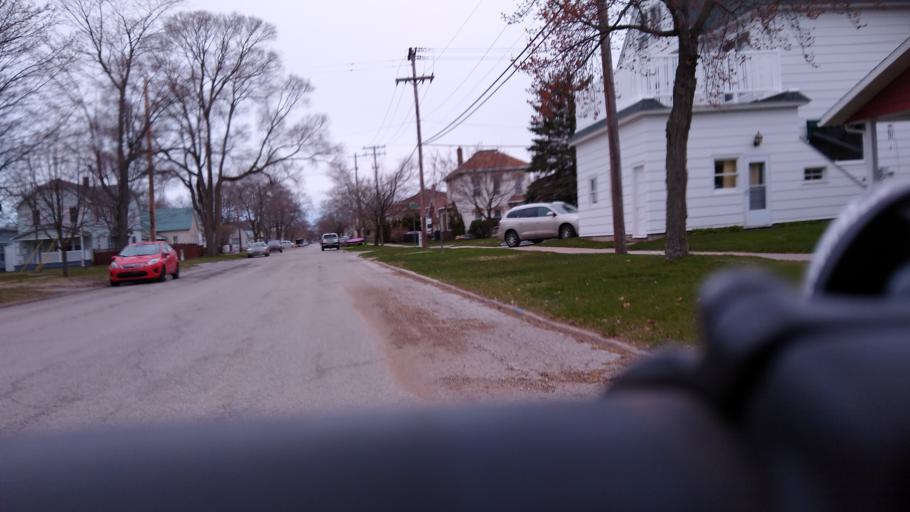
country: US
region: Michigan
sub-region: Delta County
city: Escanaba
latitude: 45.7422
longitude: -87.0560
